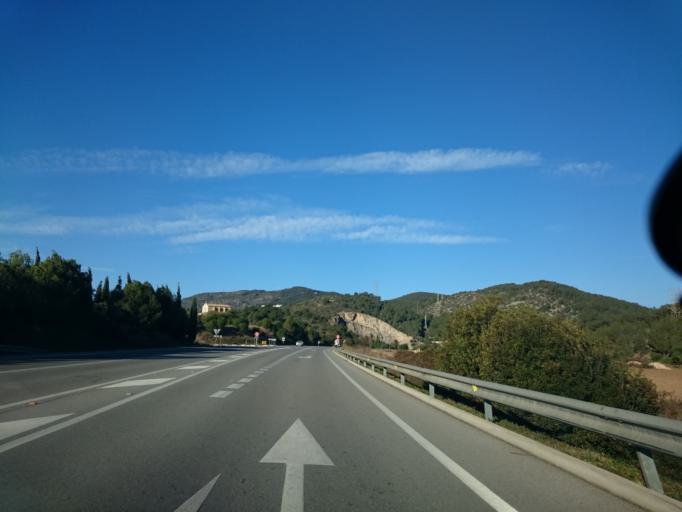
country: ES
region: Catalonia
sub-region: Provincia de Barcelona
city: Sant Pere de Ribes
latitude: 41.2664
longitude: 1.7718
